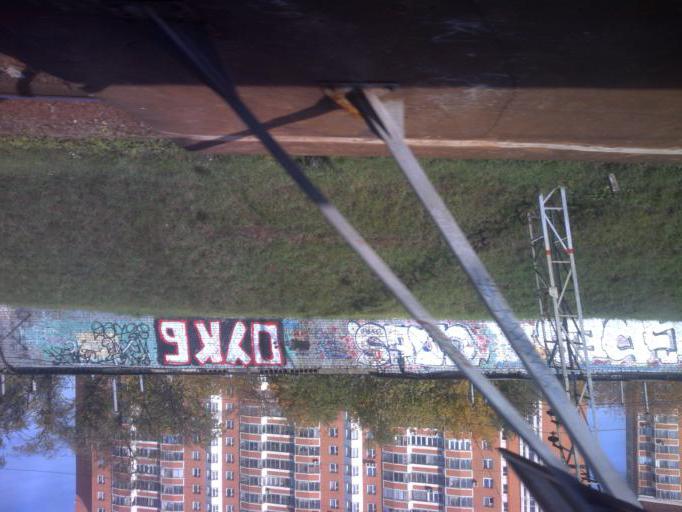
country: RU
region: Moscow
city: Annino
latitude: 55.5915
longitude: 37.6156
